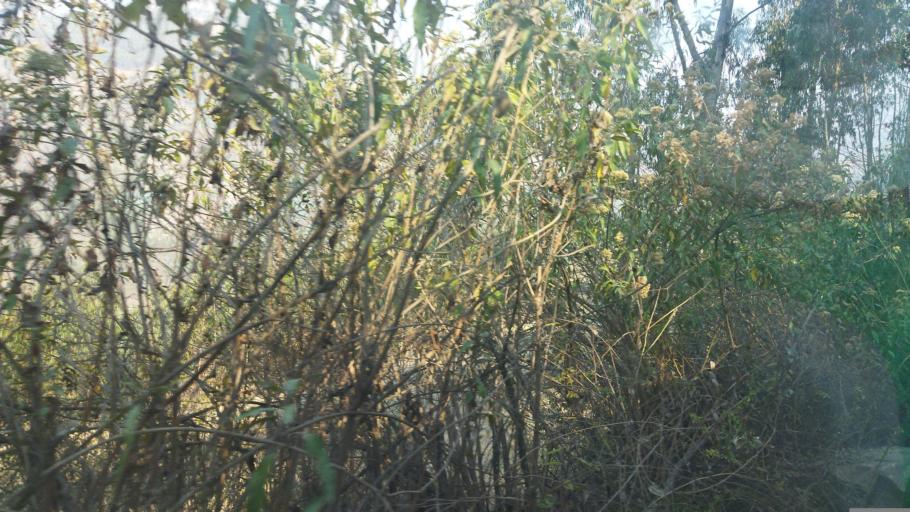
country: BO
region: La Paz
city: Quime
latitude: -16.9798
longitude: -67.1965
